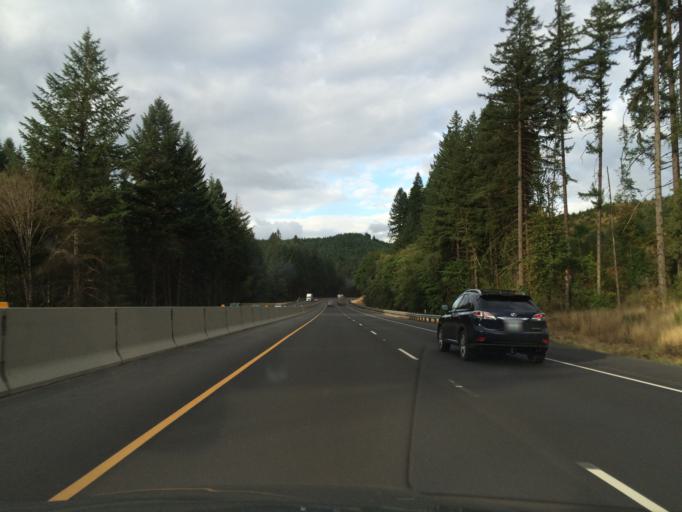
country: US
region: Oregon
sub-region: Lane County
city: Cottage Grove
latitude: 43.7470
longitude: -123.1790
